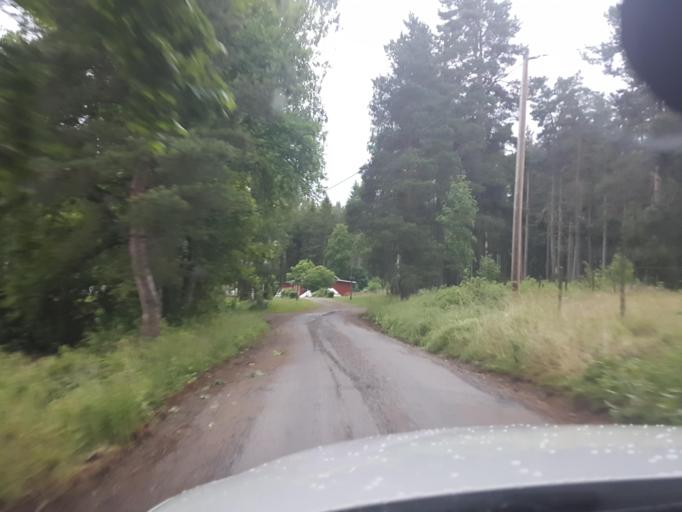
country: SE
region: Gaevleborg
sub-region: Bollnas Kommun
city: Kilafors
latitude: 61.2544
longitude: 16.6551
